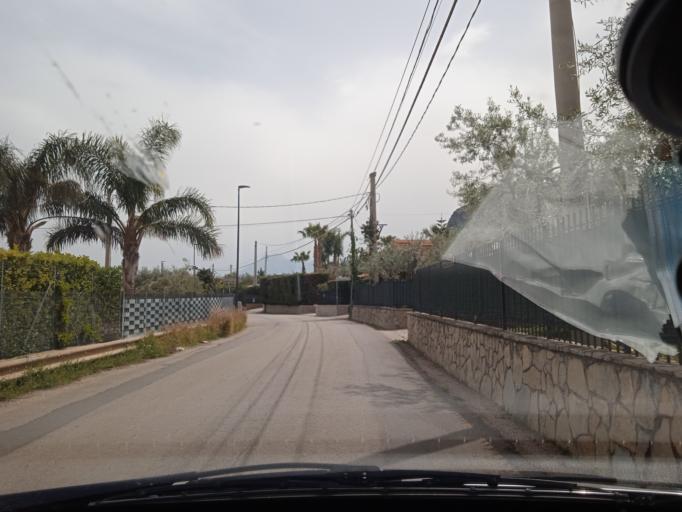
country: IT
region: Sicily
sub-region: Palermo
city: Torre Colonna-Sperone
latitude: 38.0294
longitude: 13.5701
